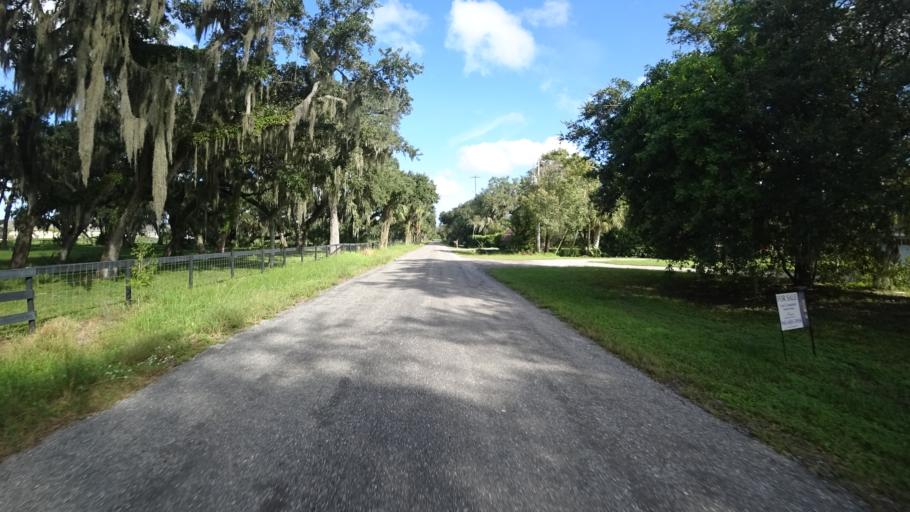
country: US
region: Florida
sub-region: Manatee County
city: Ellenton
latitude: 27.5769
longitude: -82.5029
